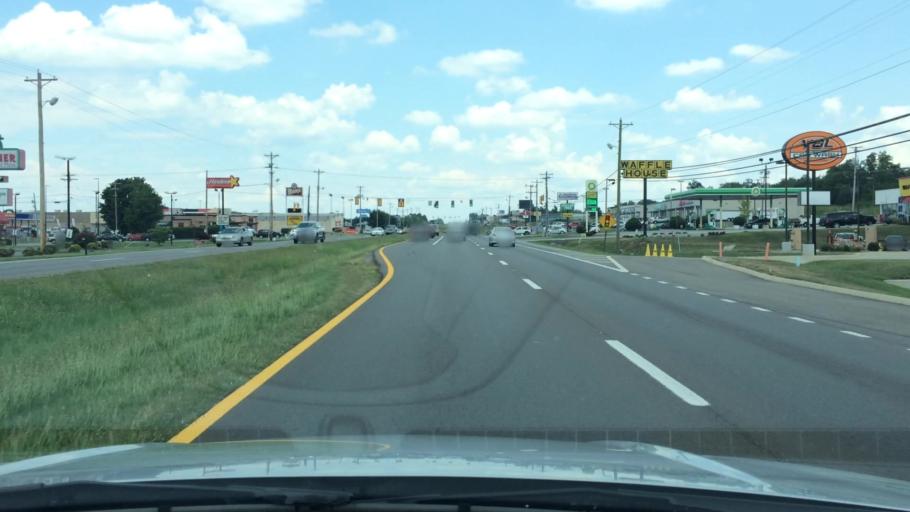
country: US
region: Tennessee
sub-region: Jefferson County
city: Jefferson City
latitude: 36.1252
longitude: -83.4704
